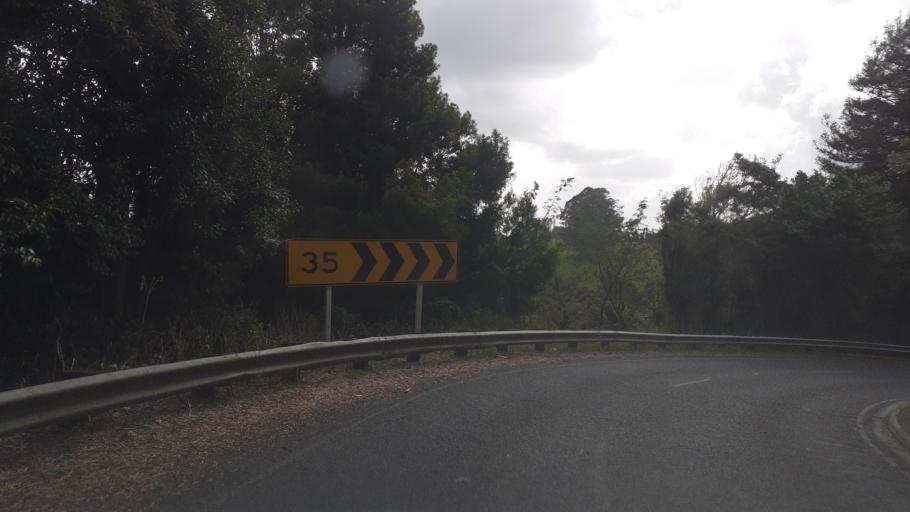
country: NZ
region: Northland
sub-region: Far North District
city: Kerikeri
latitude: -35.2165
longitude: 173.9835
